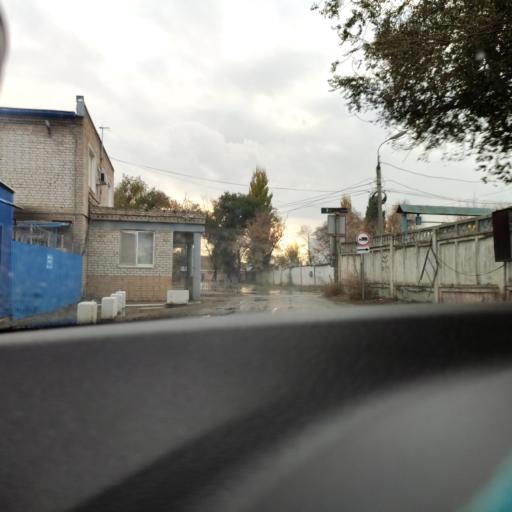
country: RU
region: Samara
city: Samara
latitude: 53.2017
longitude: 50.2555
